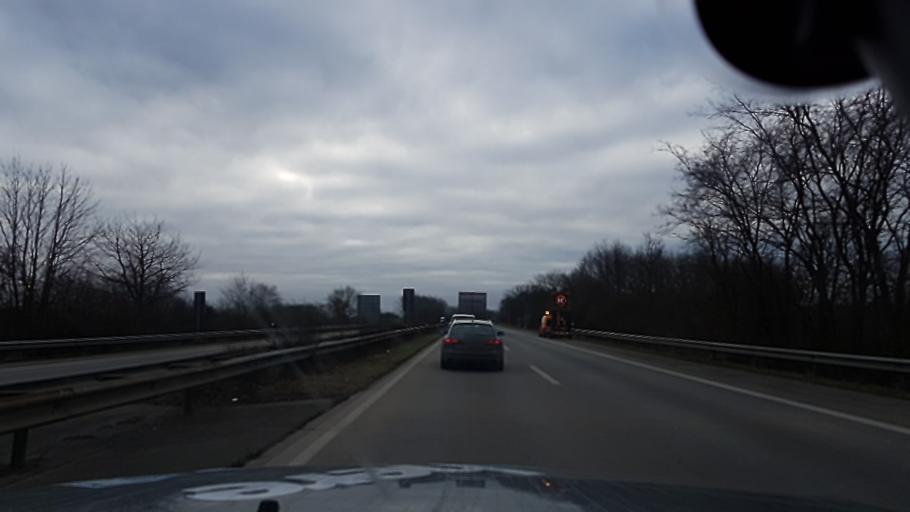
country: DE
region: Schleswig-Holstein
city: Scharbeutz
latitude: 53.9984
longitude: 10.7312
